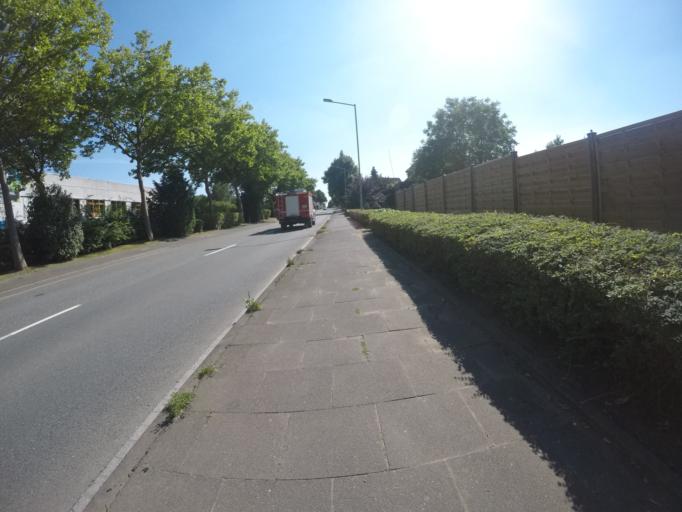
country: DE
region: North Rhine-Westphalia
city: Bad Oeynhausen
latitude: 52.1828
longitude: 8.7568
